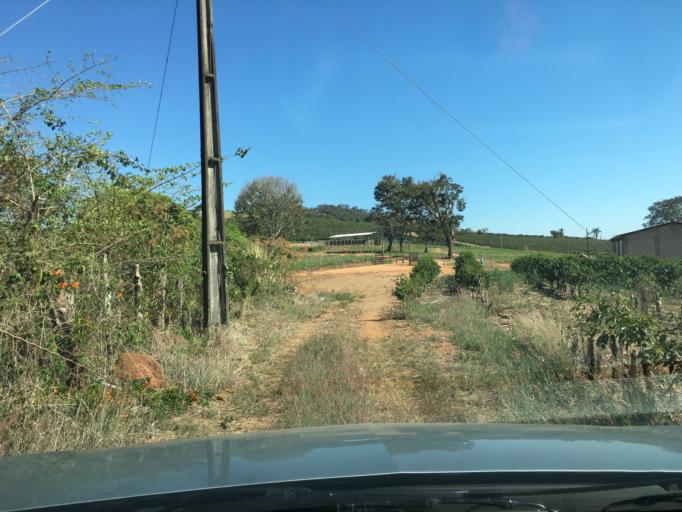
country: BR
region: Minas Gerais
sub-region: Campestre
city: Campestre
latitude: -21.5922
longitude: -46.2062
